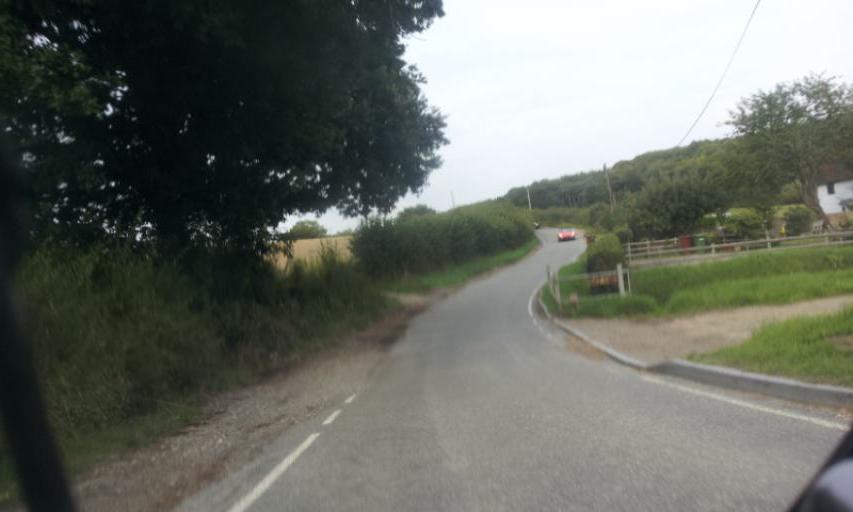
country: GB
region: England
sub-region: Kent
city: Tonbridge
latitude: 51.1718
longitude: 0.2735
